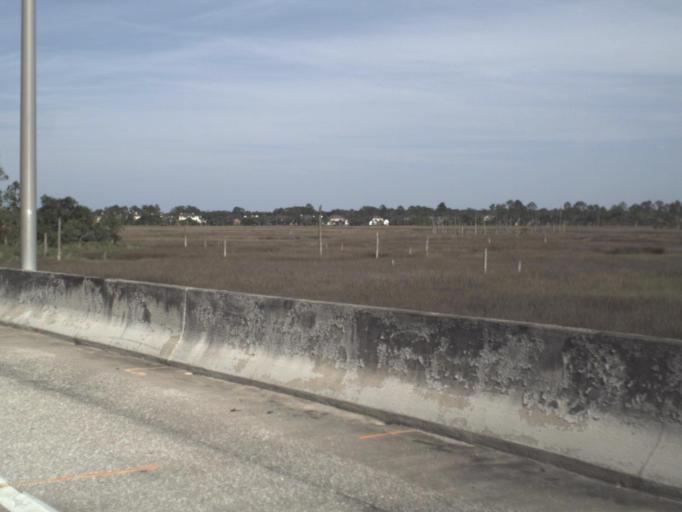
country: US
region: Florida
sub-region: Saint Johns County
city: Ponte Vedra Beach
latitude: 30.2579
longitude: -81.4185
